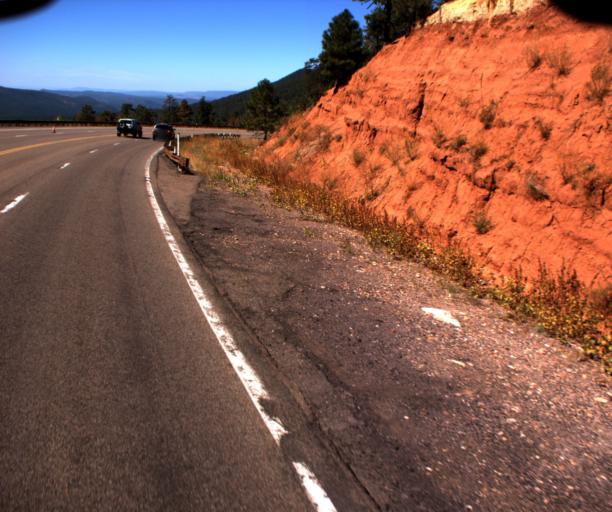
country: US
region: Arizona
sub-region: Gila County
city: Star Valley
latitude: 34.3031
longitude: -110.9179
